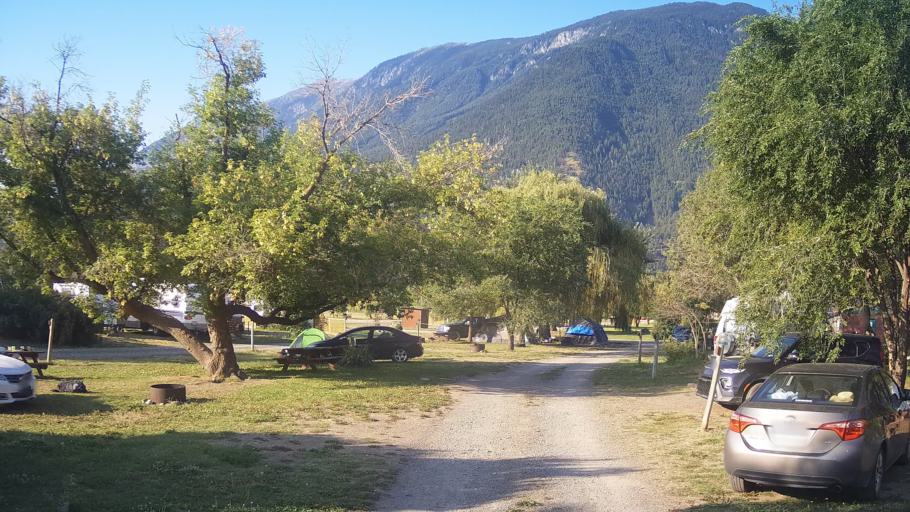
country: CA
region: British Columbia
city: Lillooet
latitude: 50.6820
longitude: -121.9317
